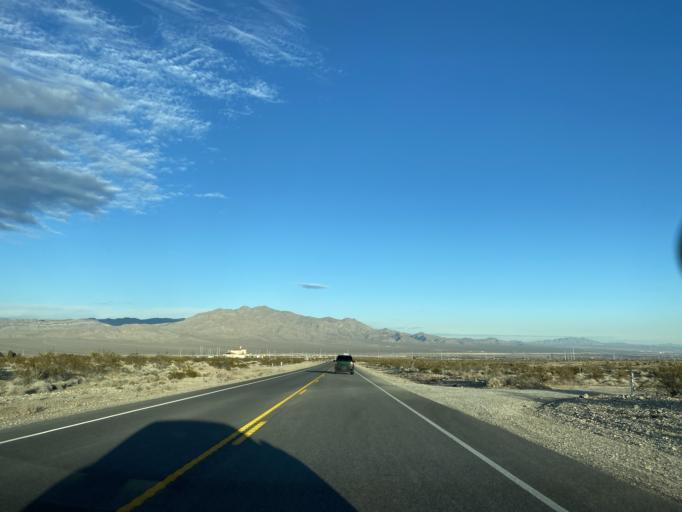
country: US
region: Nevada
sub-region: Clark County
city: Summerlin South
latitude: 36.3214
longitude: -115.3542
